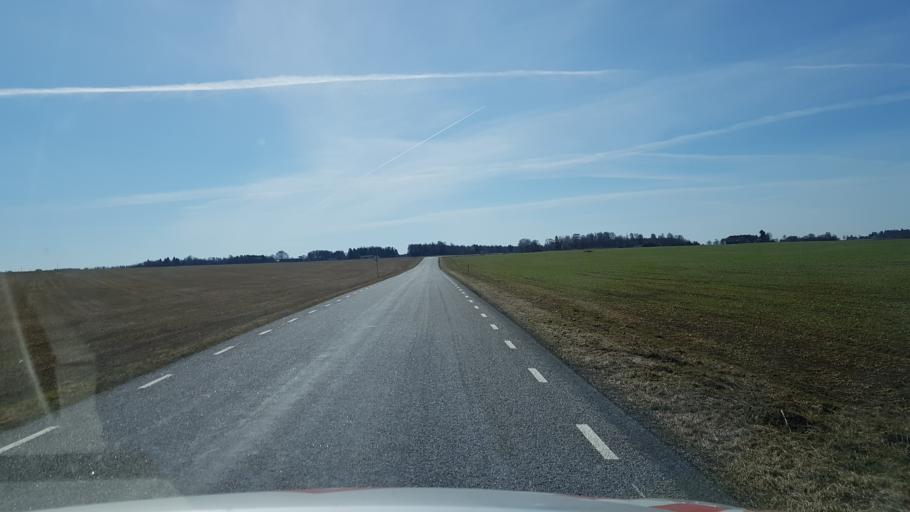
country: EE
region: Laeaene-Virumaa
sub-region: Vinni vald
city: Vinni
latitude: 59.2877
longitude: 26.3848
